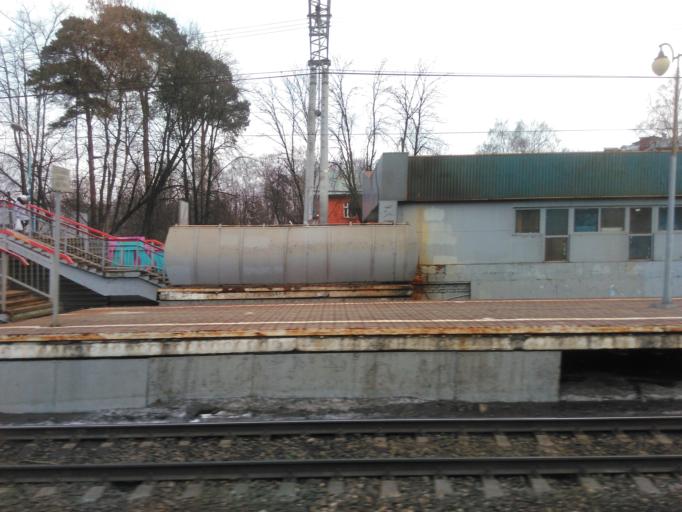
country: RU
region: Moscow
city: Yaroslavskiy
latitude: 55.8900
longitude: 37.7260
